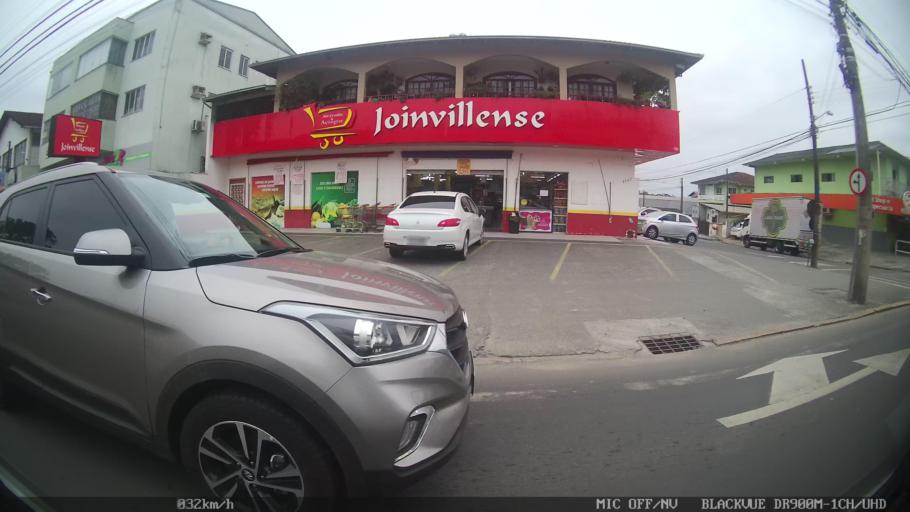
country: BR
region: Santa Catarina
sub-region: Joinville
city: Joinville
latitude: -26.3349
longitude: -48.8475
